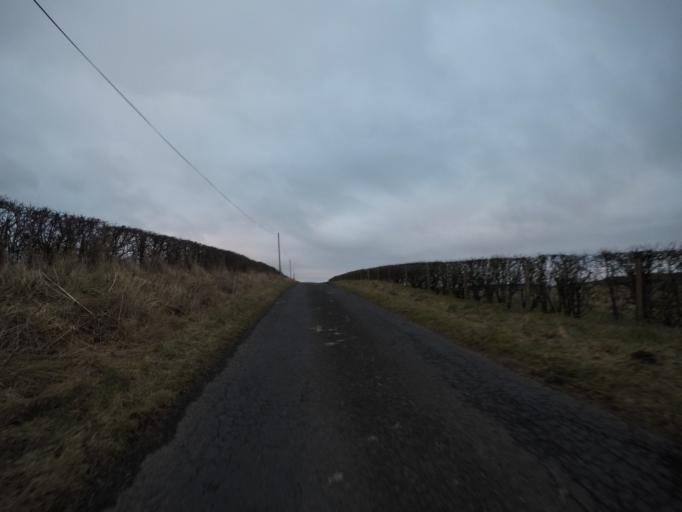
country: GB
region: Scotland
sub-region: North Ayrshire
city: Dalry
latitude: 55.6863
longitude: -4.7596
